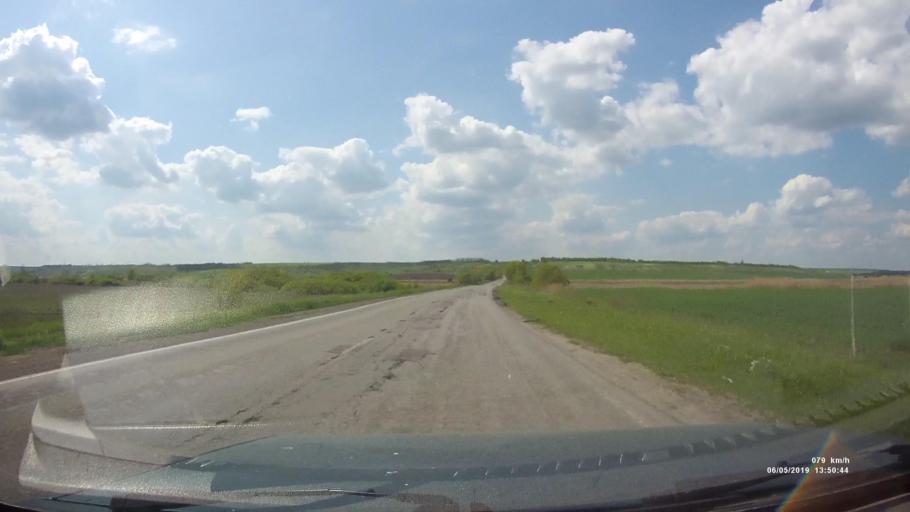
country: RU
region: Rostov
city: Melikhovskaya
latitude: 47.6545
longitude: 40.5035
